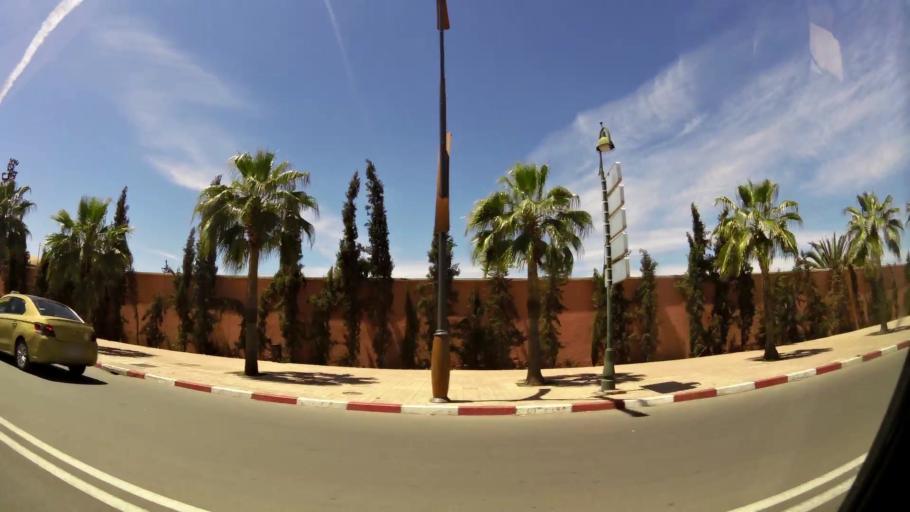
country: MA
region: Marrakech-Tensift-Al Haouz
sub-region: Marrakech
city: Marrakesh
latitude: 31.6140
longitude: -7.9928
